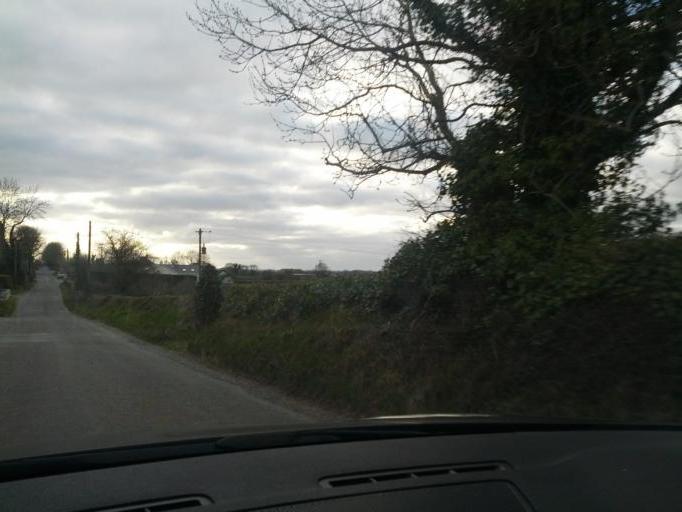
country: IE
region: Leinster
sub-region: Uibh Fhaili
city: Ferbane
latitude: 53.3233
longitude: -7.9168
